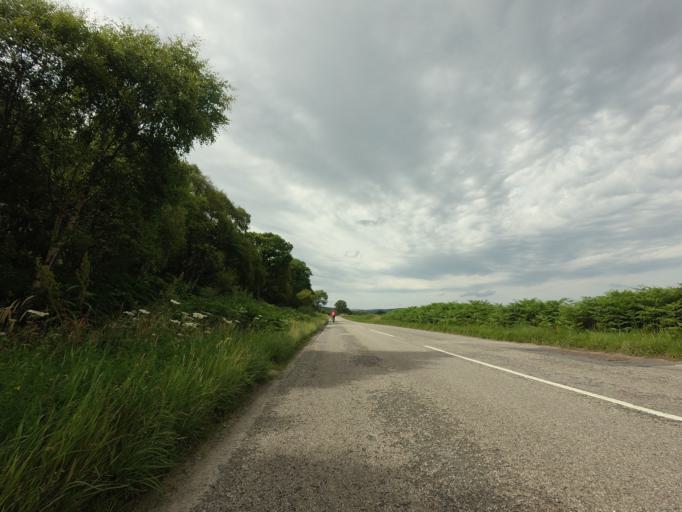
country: GB
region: Scotland
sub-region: Highland
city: Alness
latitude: 57.8697
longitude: -4.3422
